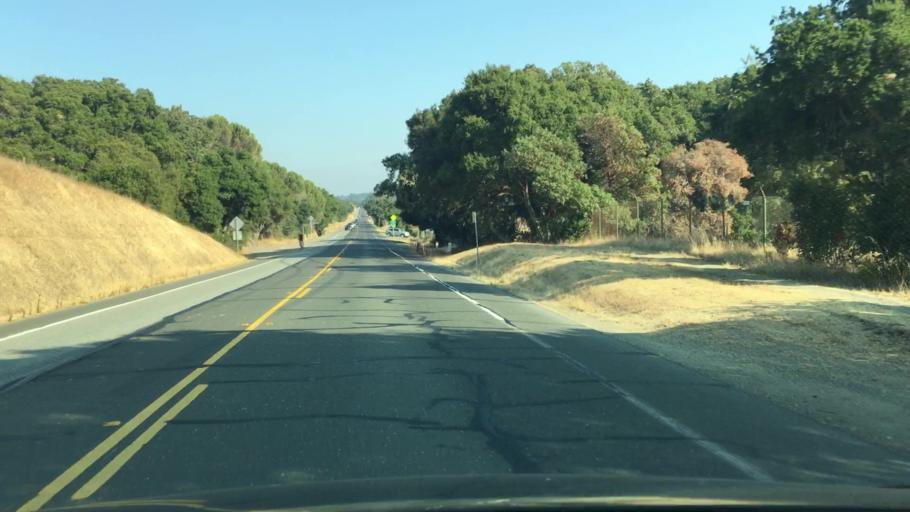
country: US
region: California
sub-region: San Mateo County
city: Emerald Lake Hills
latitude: 37.4799
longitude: -122.3121
